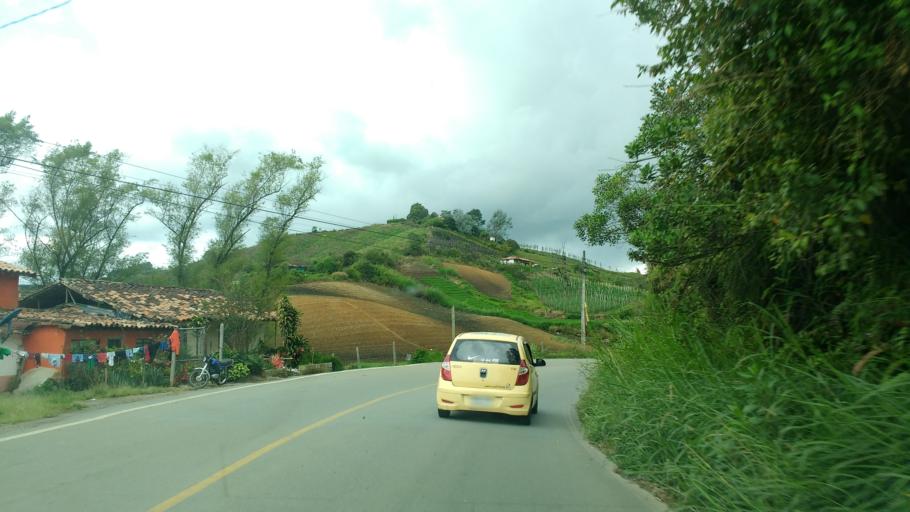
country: CO
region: Antioquia
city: Marinilla
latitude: 6.1824
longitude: -75.2972
